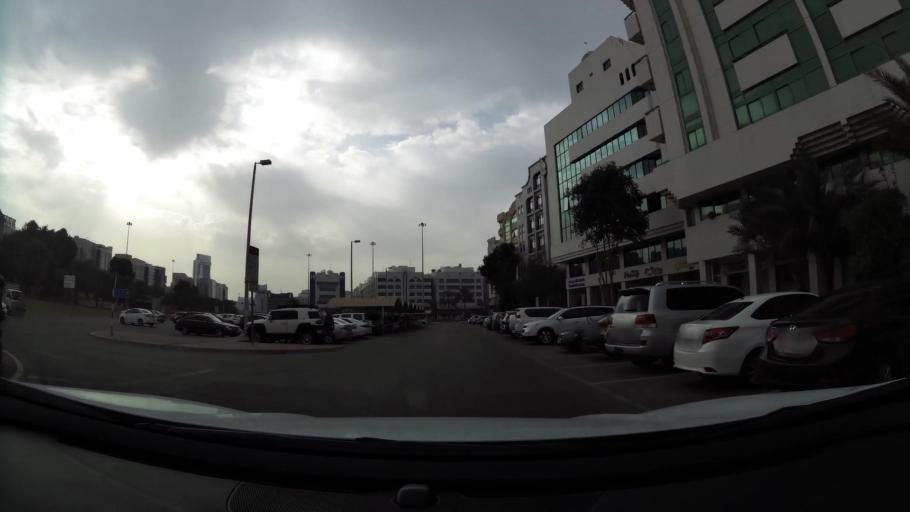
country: AE
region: Abu Dhabi
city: Abu Dhabi
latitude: 24.4672
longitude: 54.3801
